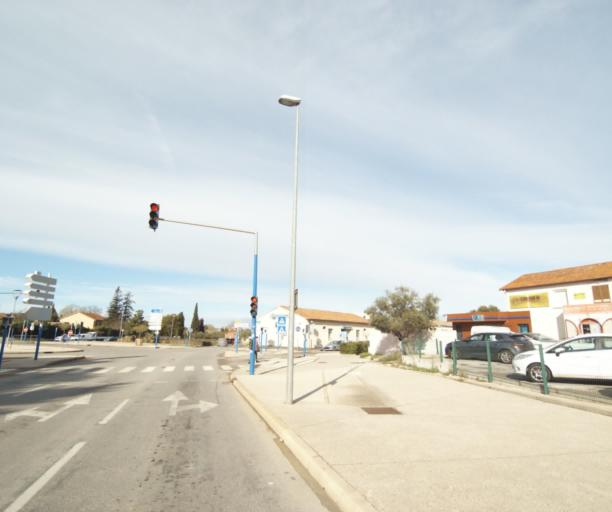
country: FR
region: Languedoc-Roussillon
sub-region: Departement de l'Herault
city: Saint-Jean-de-Vedas
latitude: 43.5757
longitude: 3.8299
